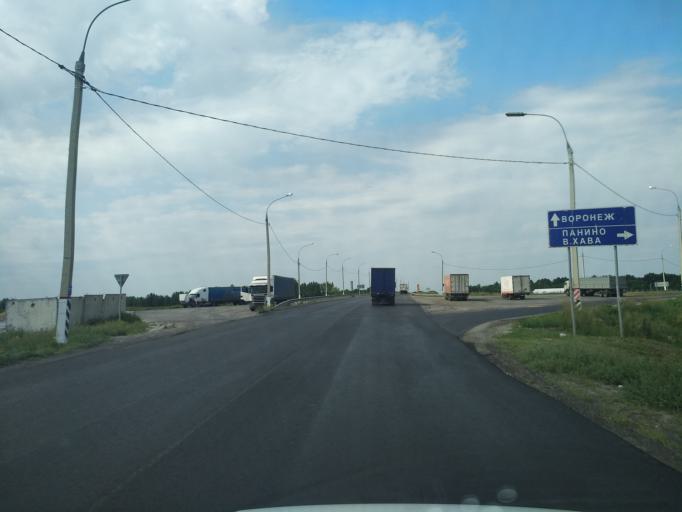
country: RU
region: Voronezj
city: Pereleshino
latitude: 51.7648
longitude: 40.1316
